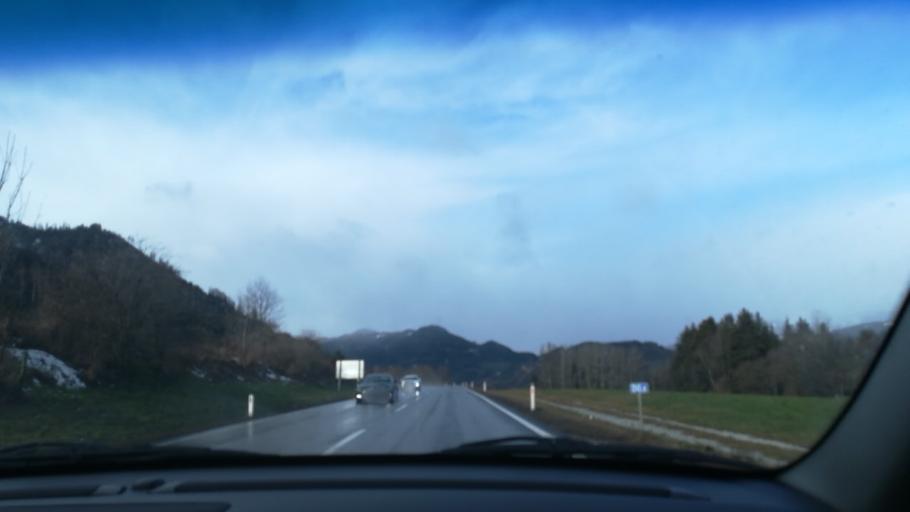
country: AT
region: Styria
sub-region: Politischer Bezirk Murtal
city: Sankt Peter ob Judenburg
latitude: 47.1877
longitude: 14.5906
